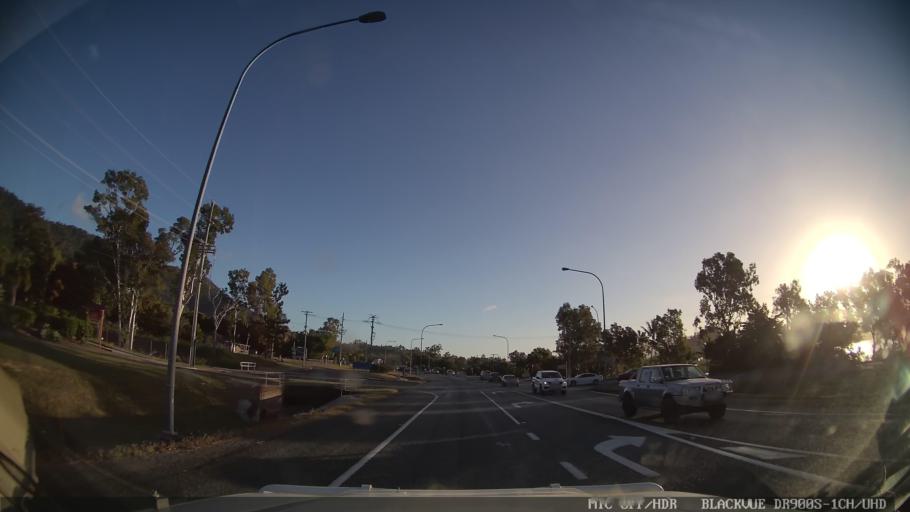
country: AU
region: Queensland
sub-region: Whitsunday
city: Proserpine
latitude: -20.2733
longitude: 148.7044
